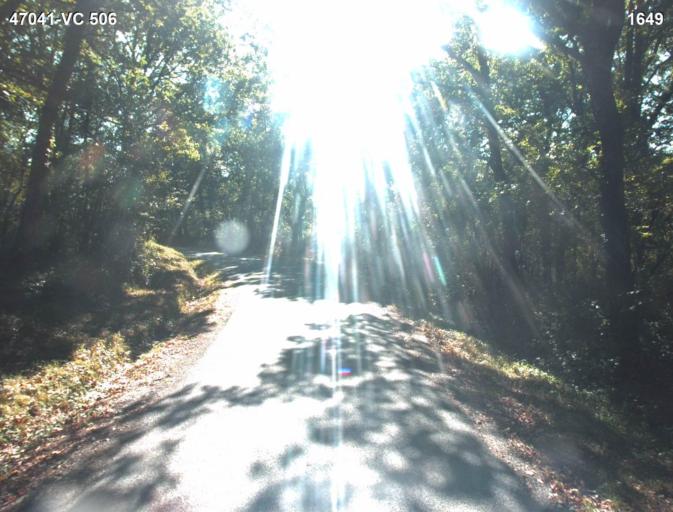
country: FR
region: Aquitaine
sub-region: Departement du Lot-et-Garonne
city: Port-Sainte-Marie
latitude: 44.2017
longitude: 0.3861
